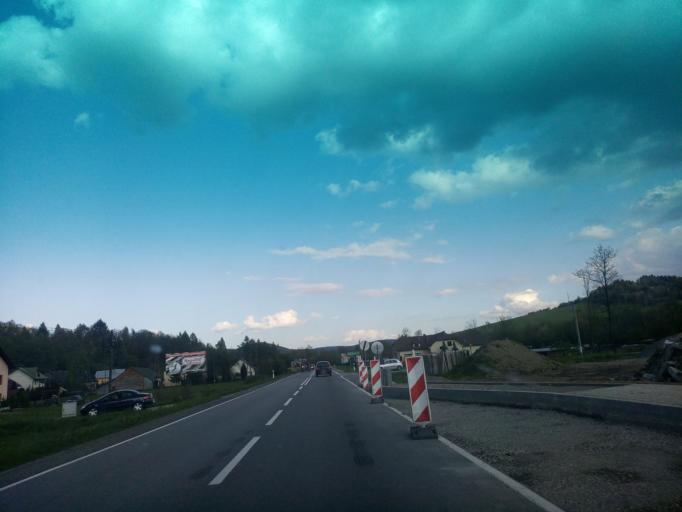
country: PL
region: Lesser Poland Voivodeship
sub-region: Powiat nowosadecki
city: Labowa
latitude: 49.5334
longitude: 20.8242
